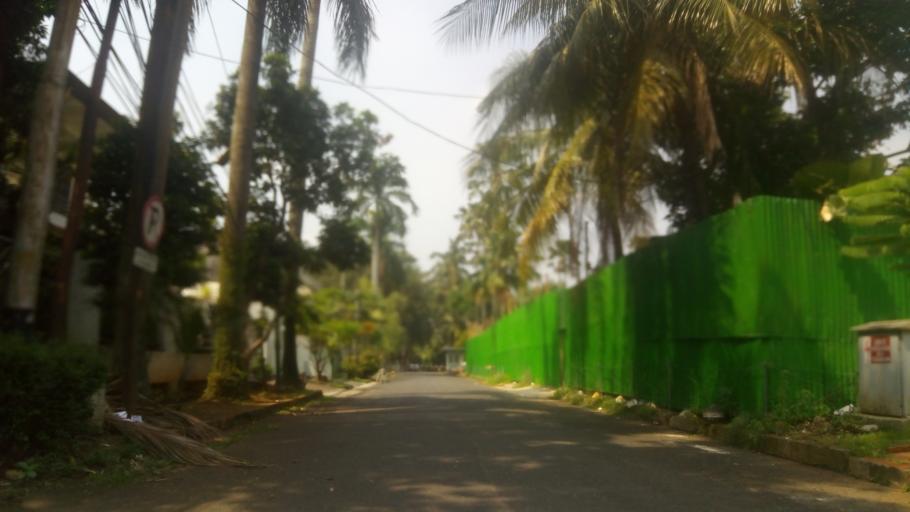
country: ID
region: Jakarta Raya
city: Jakarta
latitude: -6.2360
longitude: 106.8317
